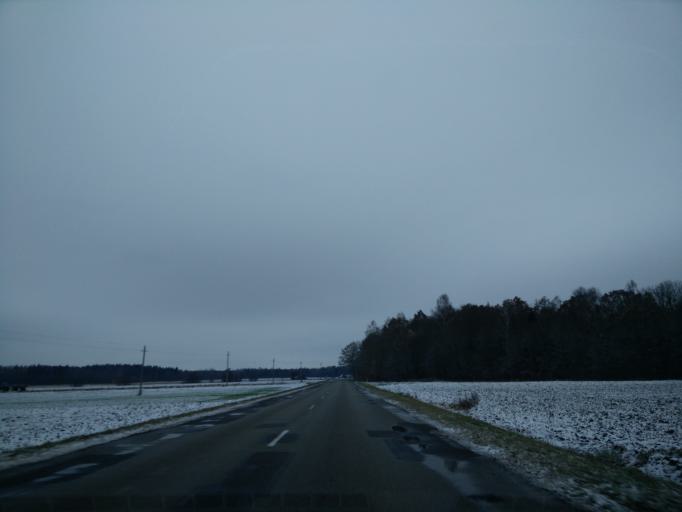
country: LT
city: Ariogala
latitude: 55.3974
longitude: 23.3396
